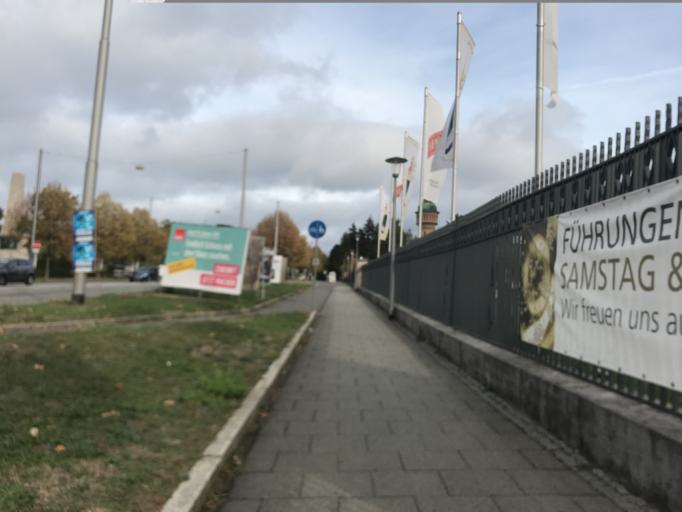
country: DE
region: Hesse
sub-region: Regierungsbezirk Darmstadt
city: Wiesbaden
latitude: 50.0535
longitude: 8.2433
